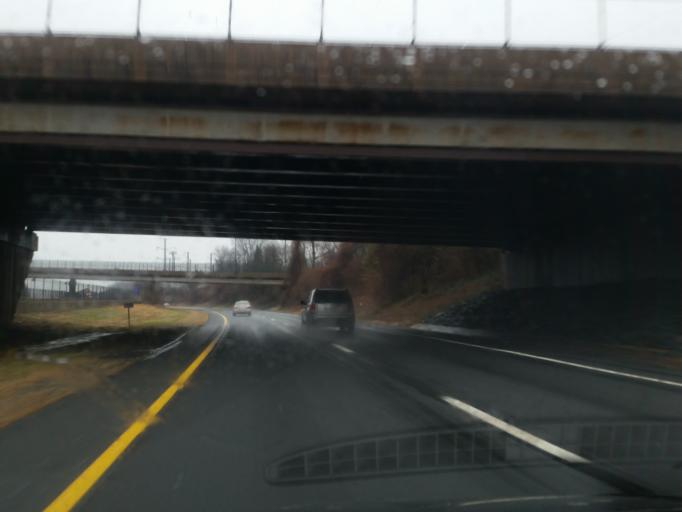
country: US
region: Virginia
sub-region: City of Falls Church
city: Falls Church
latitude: 38.8879
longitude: -77.1619
